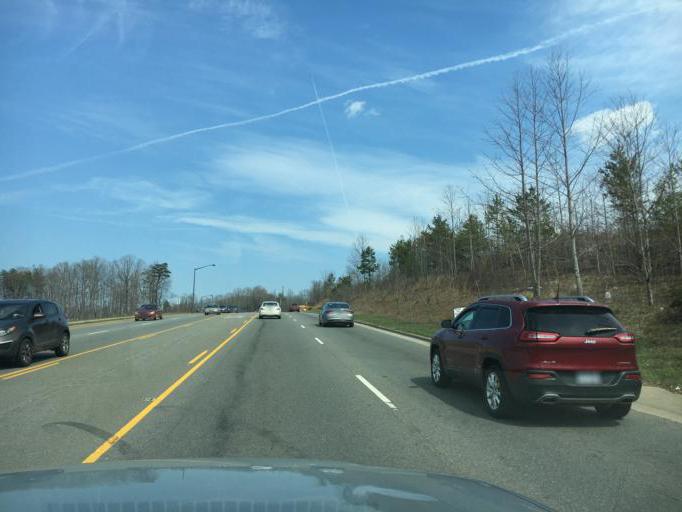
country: US
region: North Carolina
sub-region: McDowell County
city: West Marion
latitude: 35.6659
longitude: -82.0207
